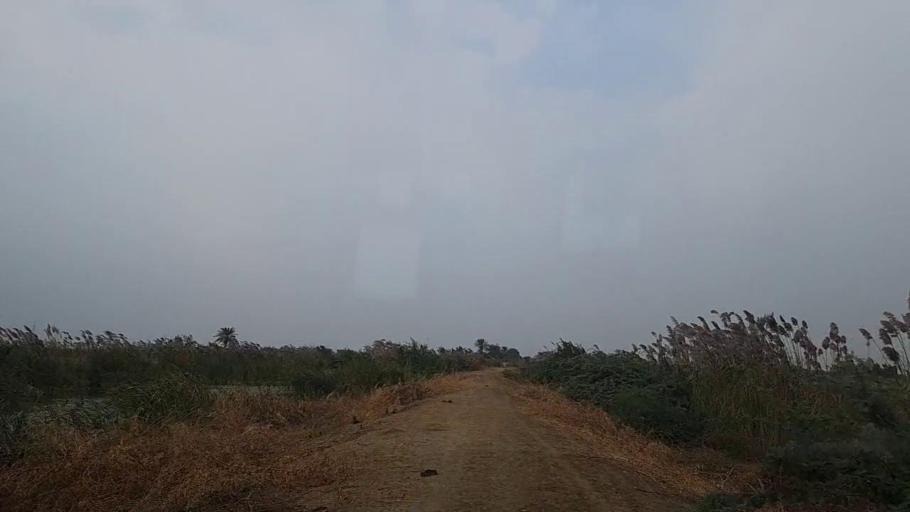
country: PK
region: Sindh
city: Gharo
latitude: 24.6258
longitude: 67.5029
